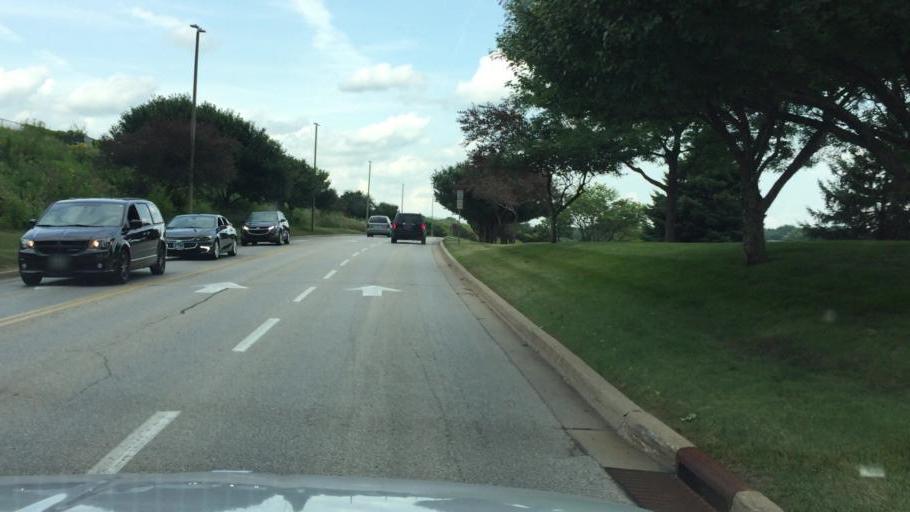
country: US
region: Iowa
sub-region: Johnson County
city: Coralville
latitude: 41.6931
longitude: -91.6041
